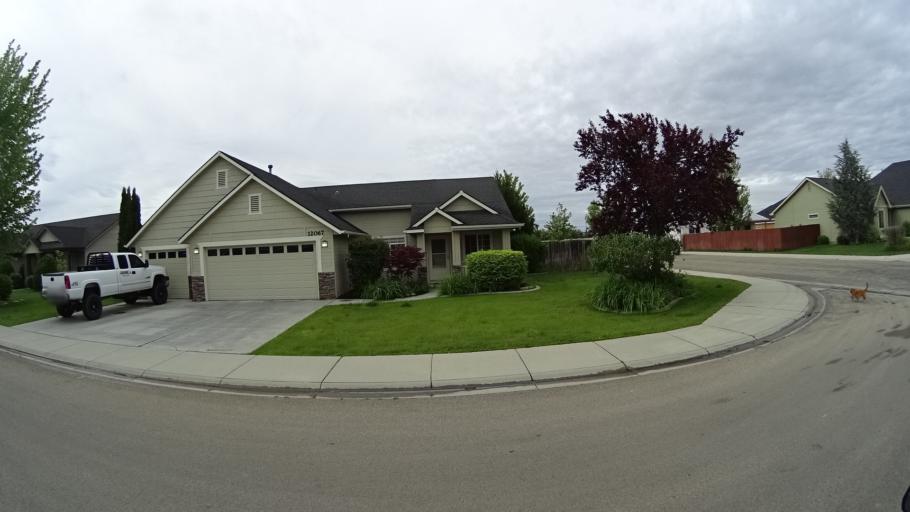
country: US
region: Idaho
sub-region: Ada County
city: Star
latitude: 43.6962
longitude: -116.5026
